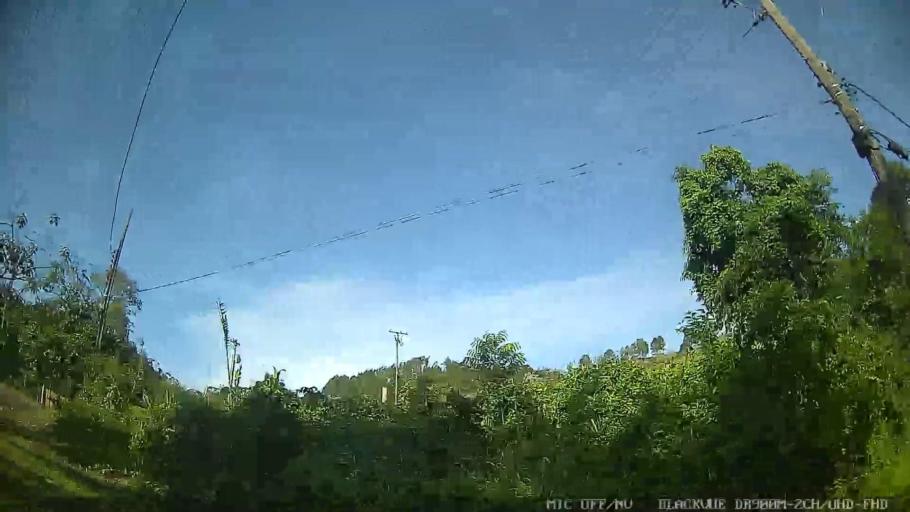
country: BR
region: Sao Paulo
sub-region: Serra Negra
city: Serra Negra
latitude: -22.6863
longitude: -46.6883
